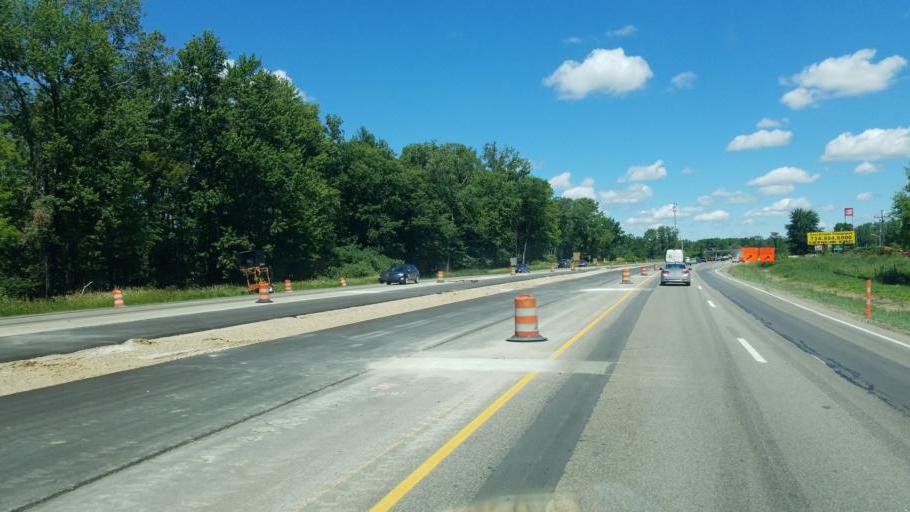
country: US
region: Michigan
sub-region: Livingston County
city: Whitmore Lake
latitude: 42.3893
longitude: -83.7624
